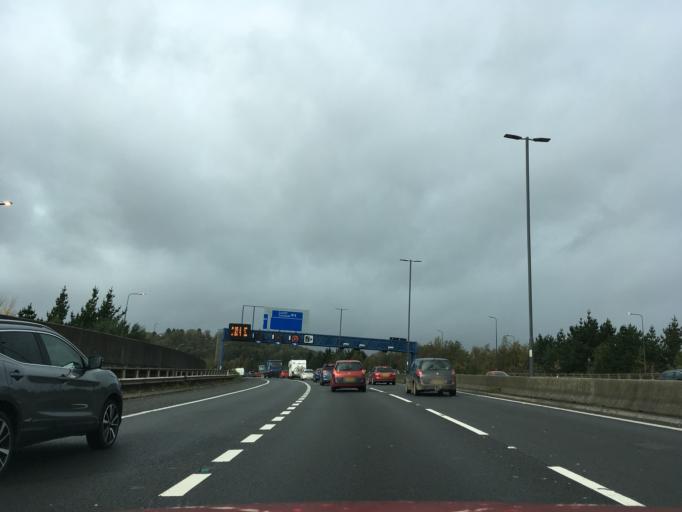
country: GB
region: Wales
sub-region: Newport
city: Newport
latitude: 51.6043
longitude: -2.9828
